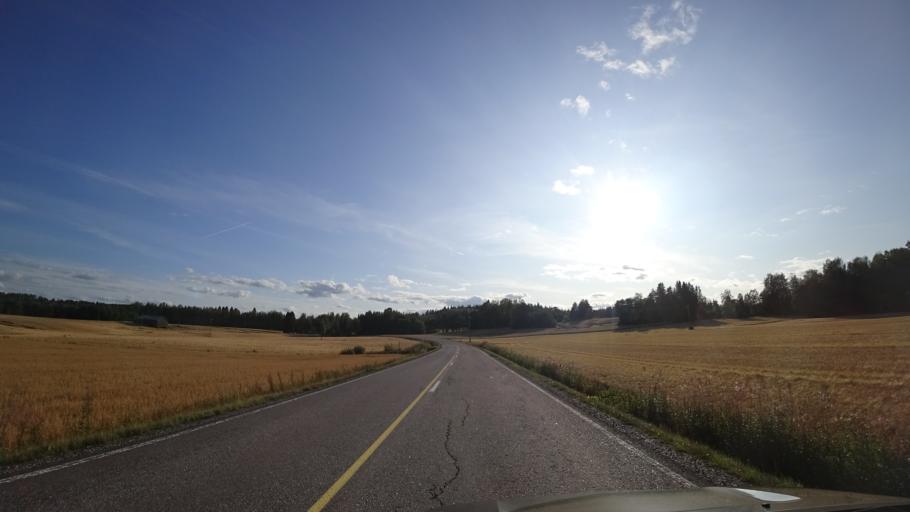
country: FI
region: Paijanne Tavastia
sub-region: Lahti
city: Asikkala
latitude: 61.1822
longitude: 25.3825
